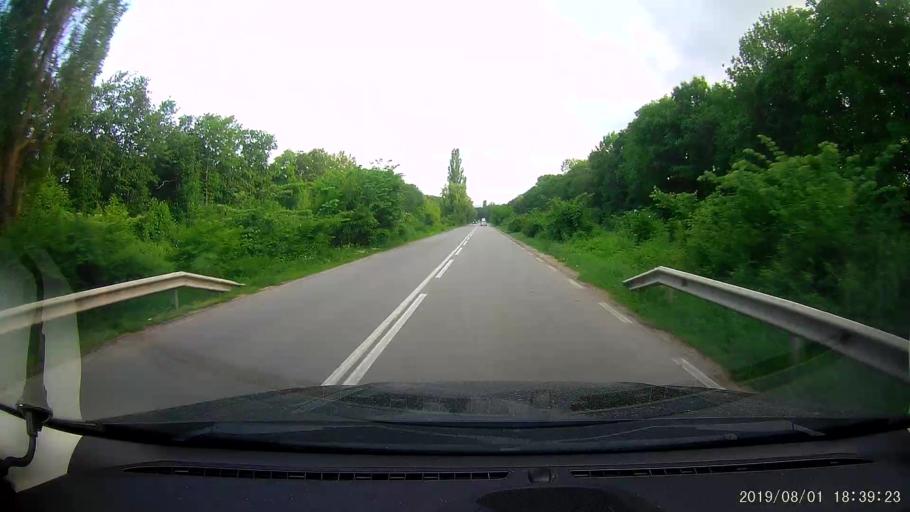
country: BG
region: Shumen
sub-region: Obshtina Khitrino
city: Gara Khitrino
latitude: 43.3869
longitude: 26.9167
